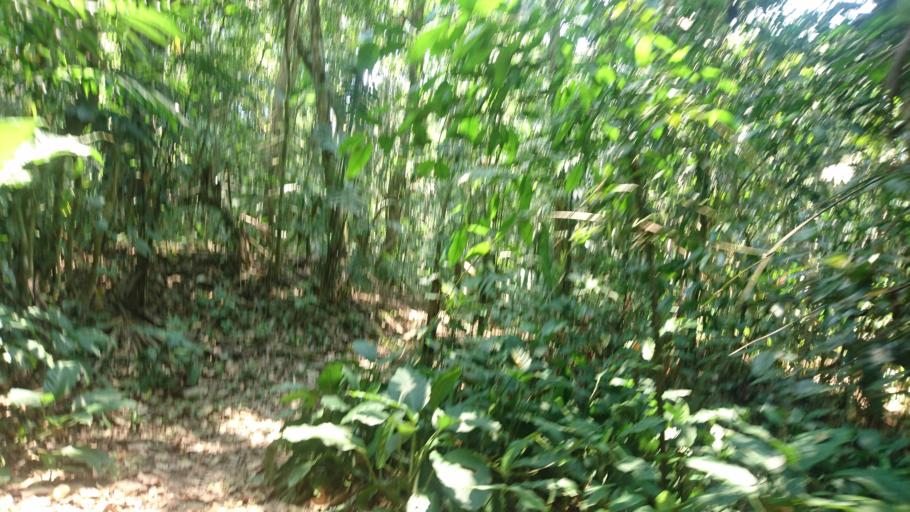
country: MX
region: Chiapas
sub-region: Marques de Comillas
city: Zamora Pico de Oro
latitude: 16.2476
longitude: -90.8312
